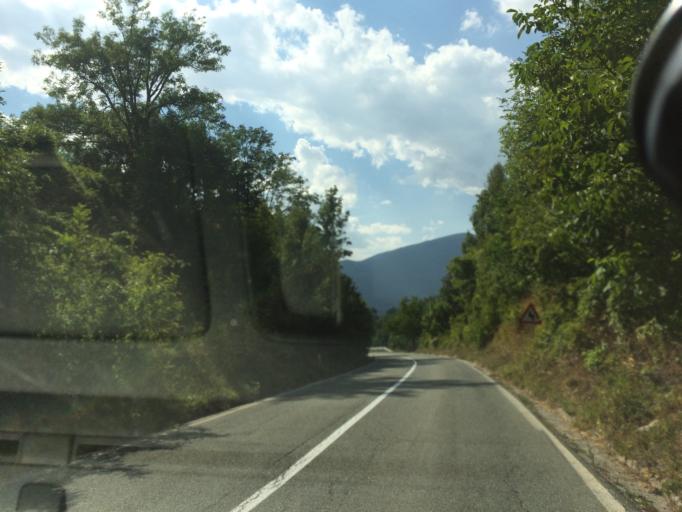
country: ME
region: Opstina Zabljak
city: Zabljak
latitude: 43.1659
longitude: 19.2891
